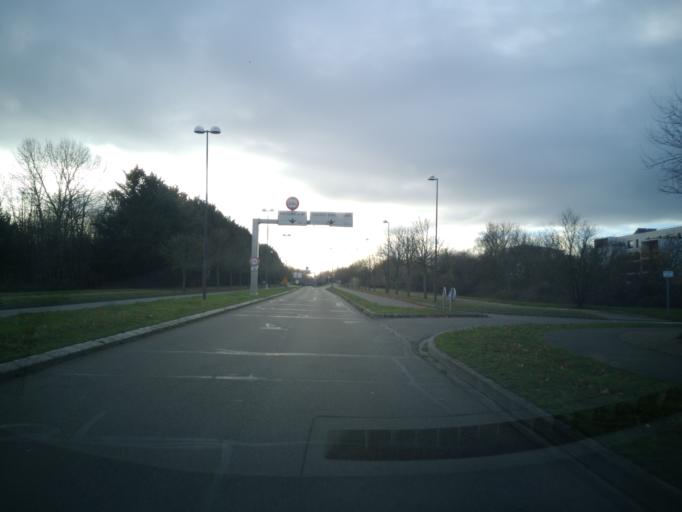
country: FR
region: Ile-de-France
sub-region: Departement des Yvelines
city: Guyancourt
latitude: 48.7640
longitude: 2.0762
